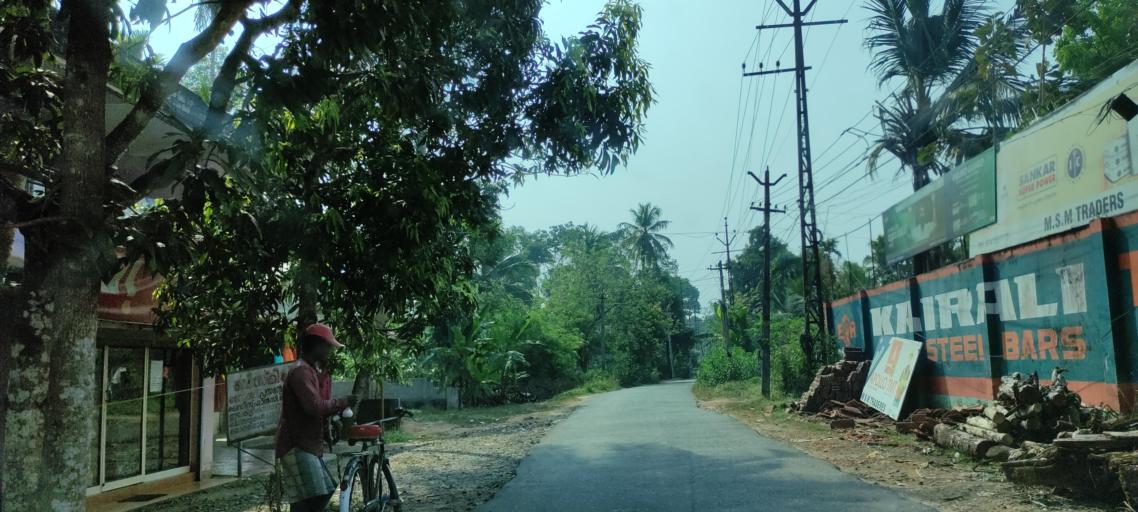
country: IN
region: Kerala
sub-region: Pattanamtitta
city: Tiruvalla
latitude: 9.3551
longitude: 76.5248
